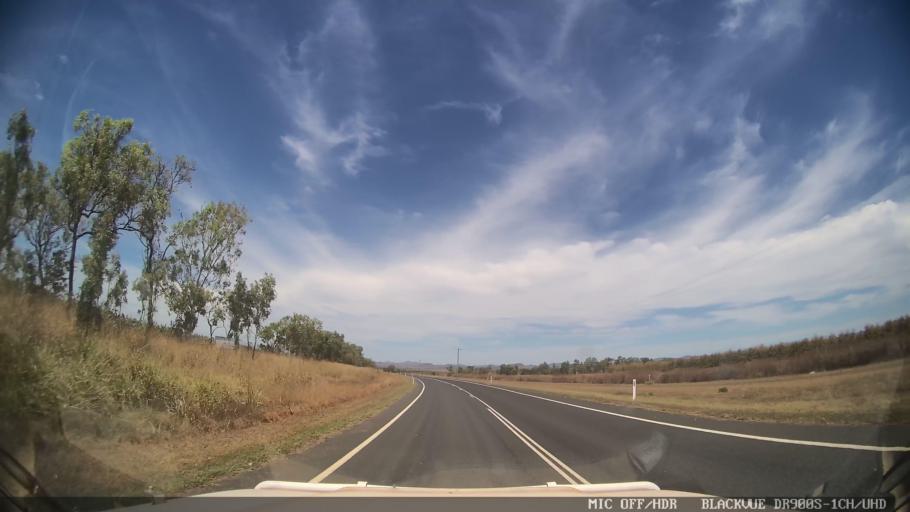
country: AU
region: Queensland
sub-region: Cook
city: Cooktown
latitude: -15.8374
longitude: 144.8532
